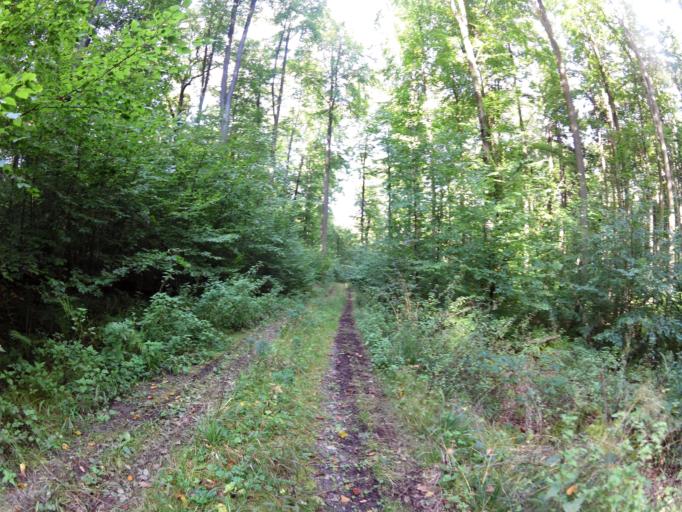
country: DE
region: Bavaria
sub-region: Regierungsbezirk Unterfranken
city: Waldbrunn
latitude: 49.7439
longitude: 9.7963
